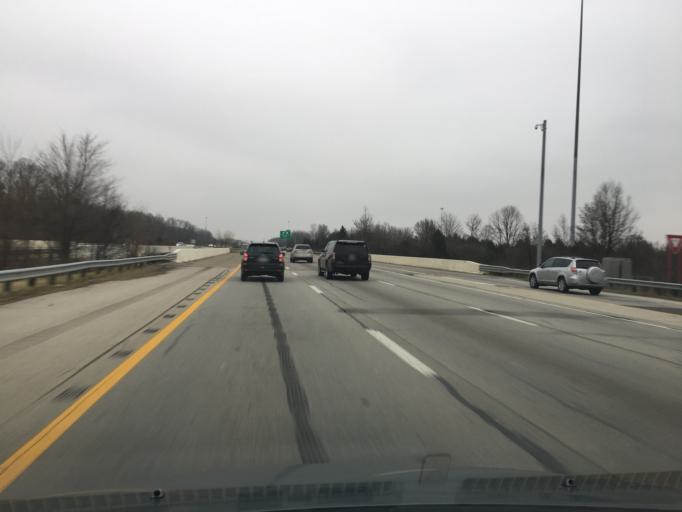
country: US
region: Ohio
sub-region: Hamilton County
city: Highpoint
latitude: 39.2717
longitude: -84.3523
